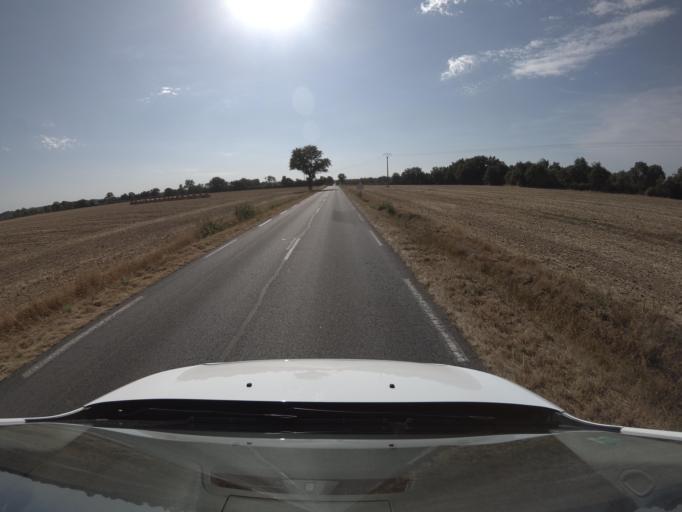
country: FR
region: Poitou-Charentes
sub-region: Departement des Deux-Sevres
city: Argenton-les-Vallees
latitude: 47.0025
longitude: -0.3689
